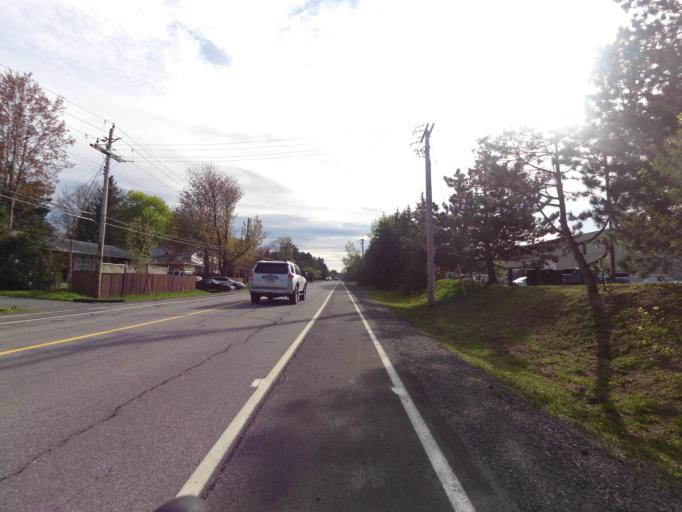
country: CA
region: Ontario
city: Ottawa
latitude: 45.3287
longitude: -75.7069
